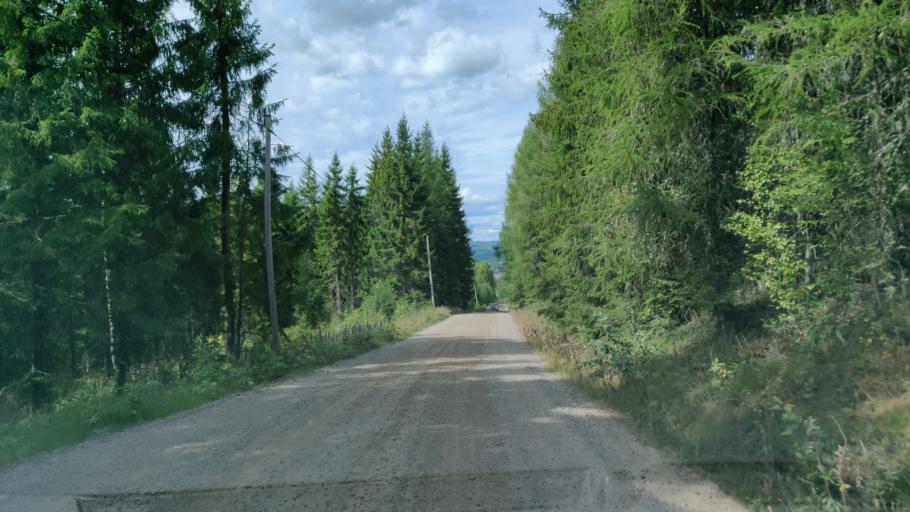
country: SE
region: Vaermland
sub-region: Hagfors Kommun
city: Hagfors
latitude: 60.0166
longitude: 13.7033
